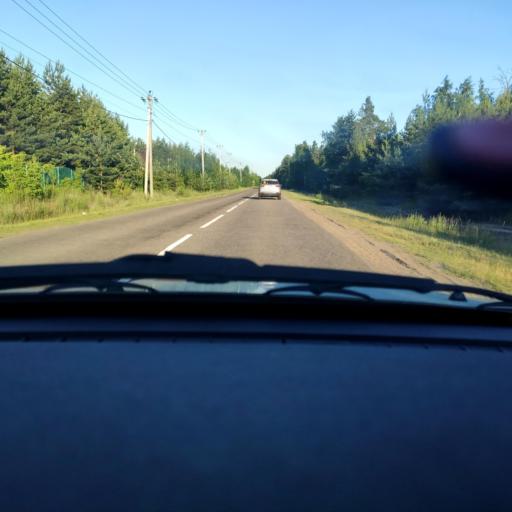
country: RU
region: Voronezj
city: Ramon'
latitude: 51.8919
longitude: 39.2434
